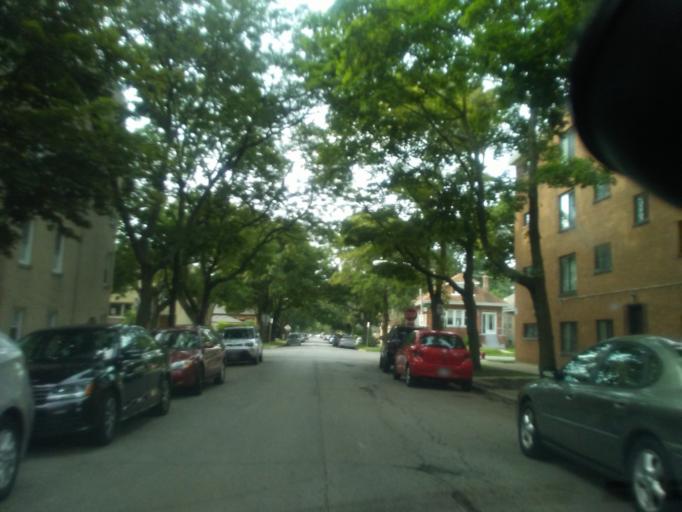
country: US
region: Illinois
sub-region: Cook County
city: Lincolnwood
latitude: 42.0090
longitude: -87.6975
